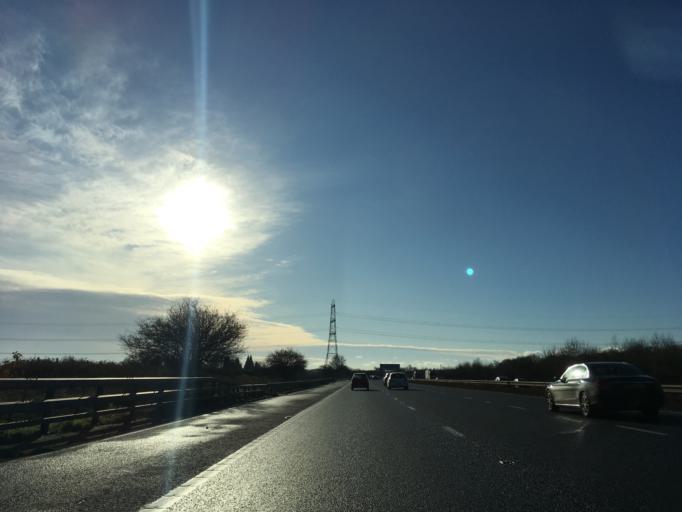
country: GB
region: England
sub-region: South Gloucestershire
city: Alveston
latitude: 51.5625
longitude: -2.5329
